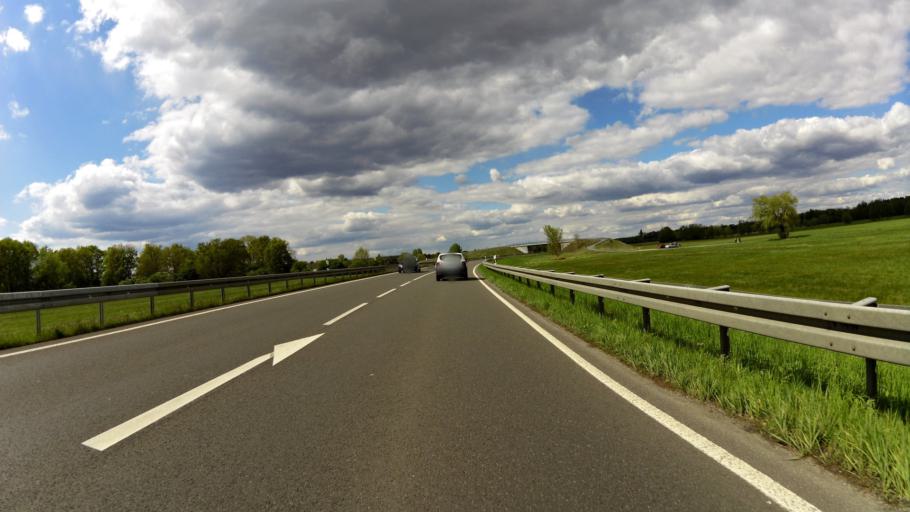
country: DE
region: Brandenburg
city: Furstenwalde
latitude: 52.3697
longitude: 14.0911
